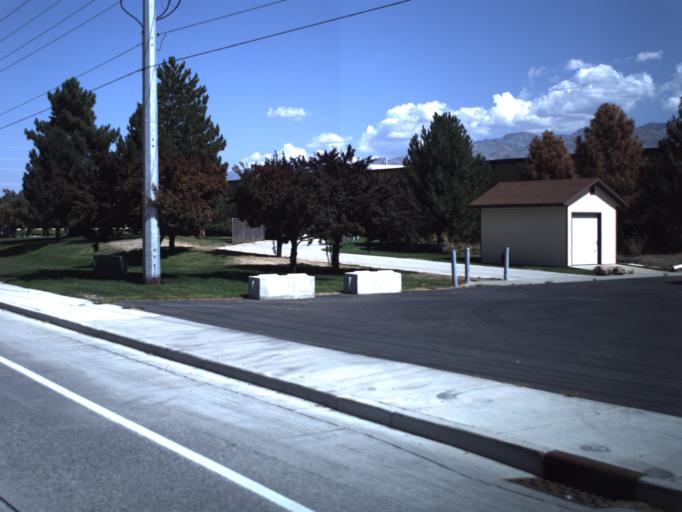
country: US
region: Utah
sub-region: Cache County
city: Logan
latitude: 41.7566
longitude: -111.8588
